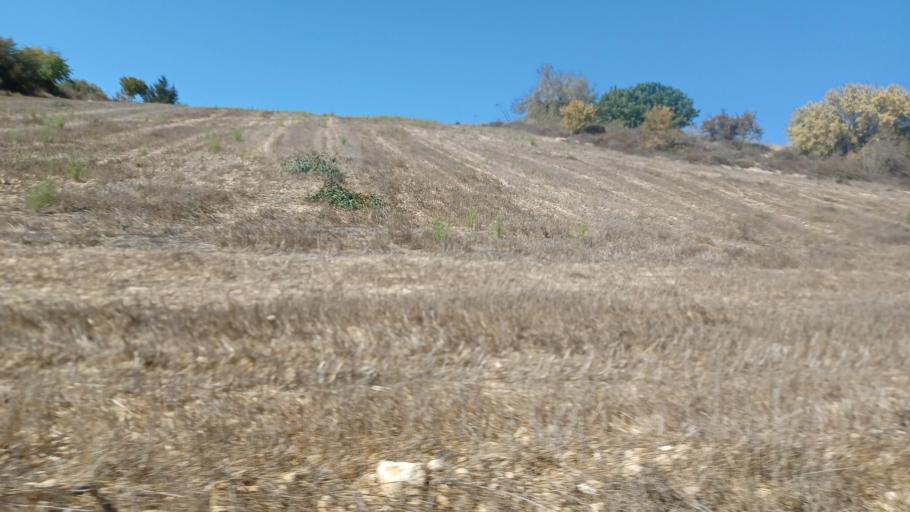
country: CY
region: Pafos
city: Mesogi
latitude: 34.8039
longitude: 32.4869
